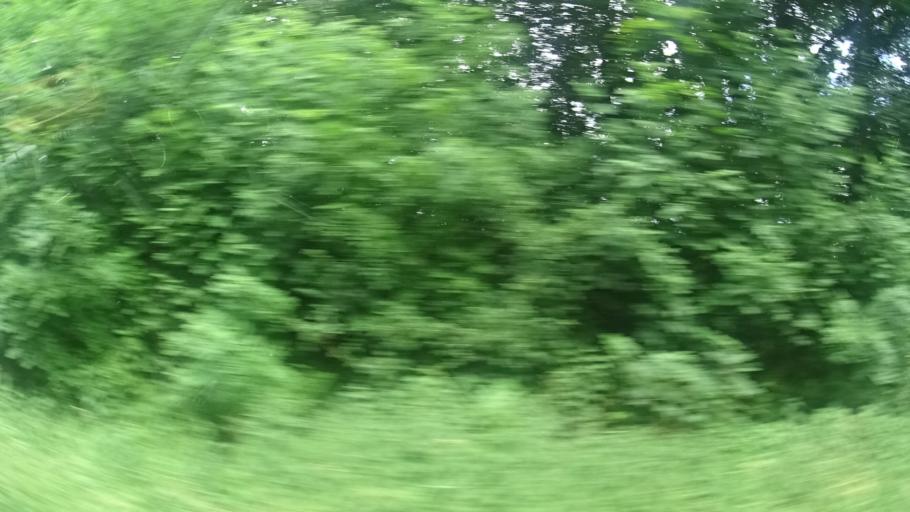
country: DE
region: Lower Saxony
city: Springe
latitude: 52.2211
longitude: 9.6253
